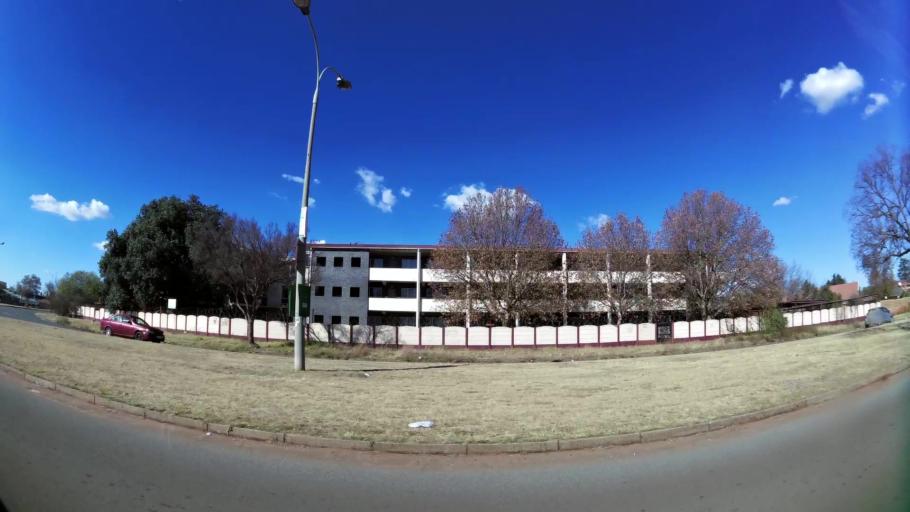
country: ZA
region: Gauteng
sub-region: West Rand District Municipality
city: Carletonville
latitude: -26.3606
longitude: 27.3943
